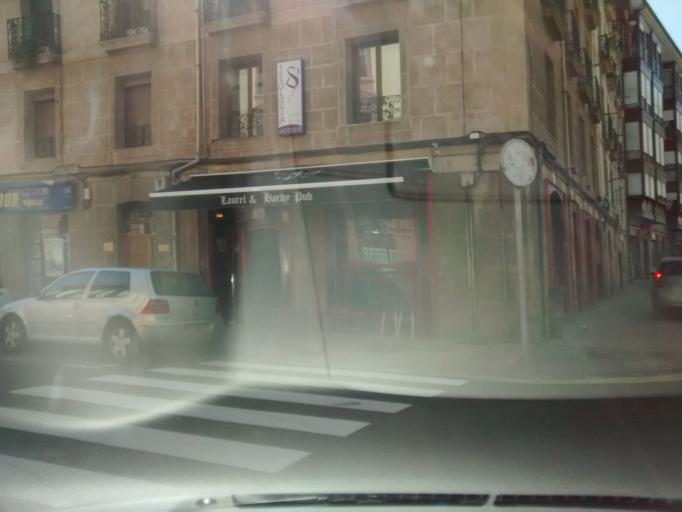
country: ES
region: Basque Country
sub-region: Provincia de Guipuzcoa
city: Eibar
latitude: 43.1846
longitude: -2.4738
